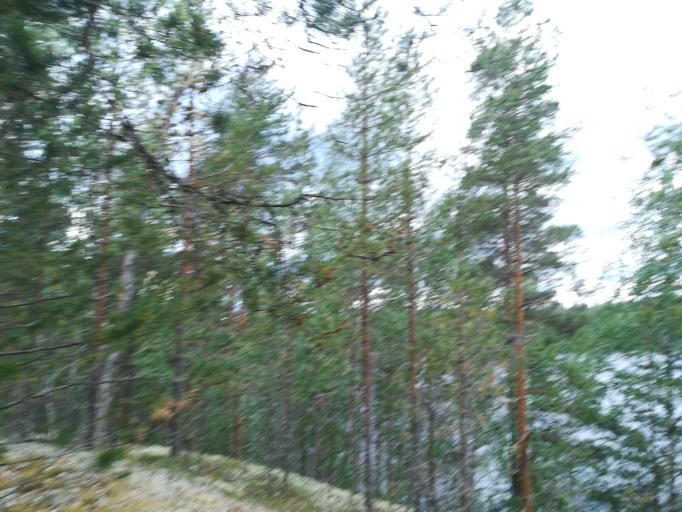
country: FI
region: Southern Savonia
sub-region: Mikkeli
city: Hirvensalmi
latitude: 61.7072
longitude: 26.9712
